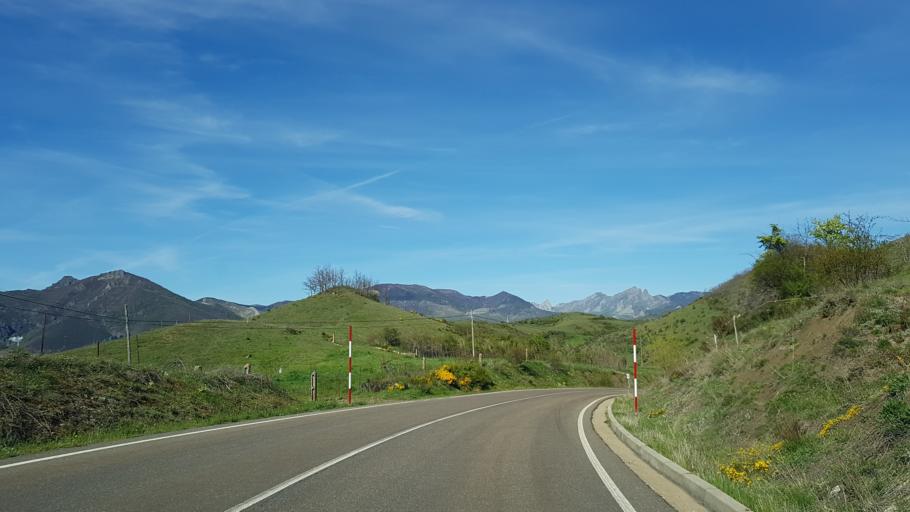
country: ES
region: Castille and Leon
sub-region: Provincia de Leon
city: Villamanin
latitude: 42.9508
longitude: -5.6317
